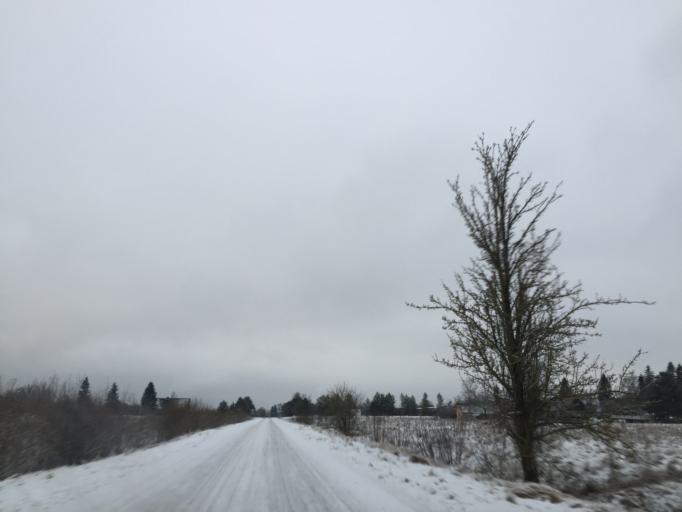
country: EE
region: Laeaene
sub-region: Lihula vald
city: Lihula
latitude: 58.6754
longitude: 23.8329
